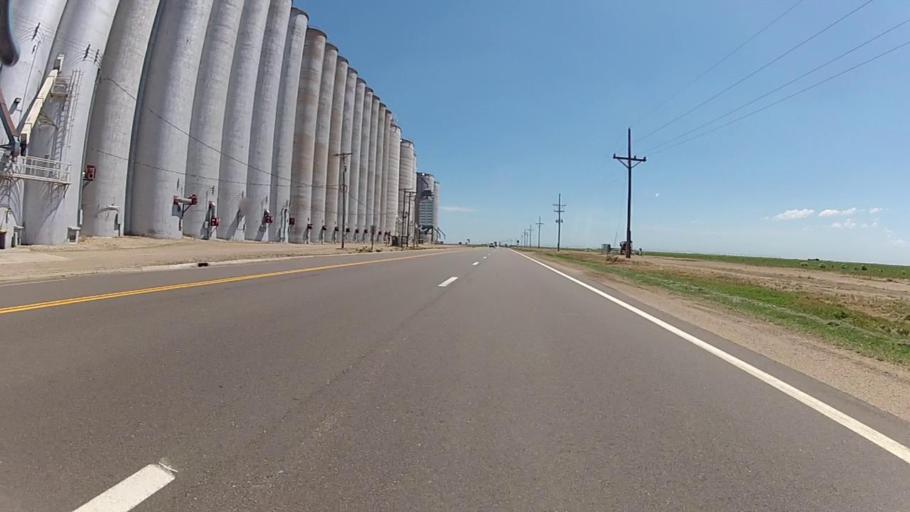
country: US
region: Kansas
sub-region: Gray County
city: Cimarron
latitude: 37.6557
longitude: -100.2278
